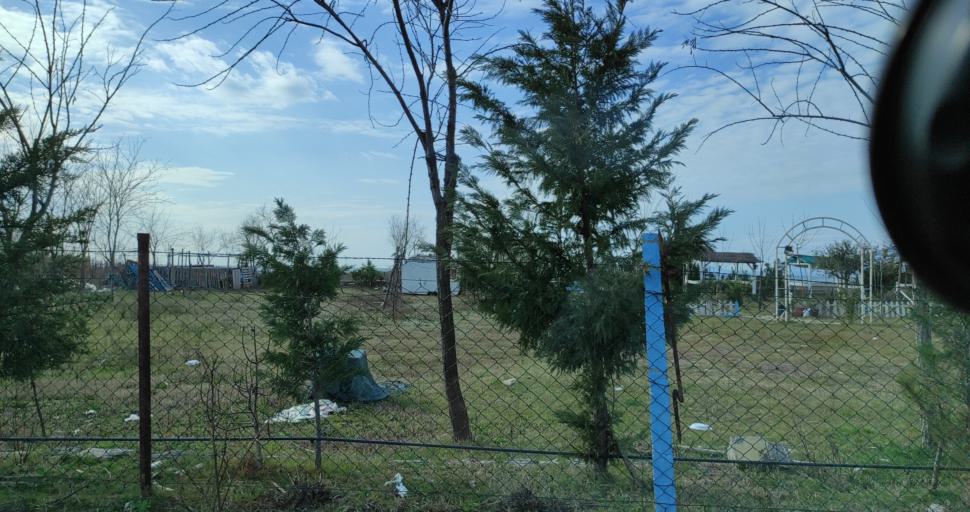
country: AL
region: Lezhe
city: Shengjin
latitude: 41.7729
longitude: 19.6022
